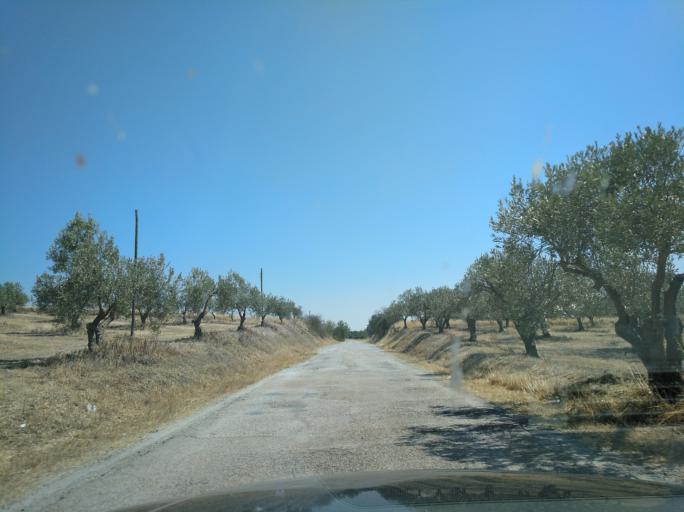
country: PT
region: Portalegre
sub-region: Campo Maior
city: Campo Maior
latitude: 38.9849
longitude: -7.1002
